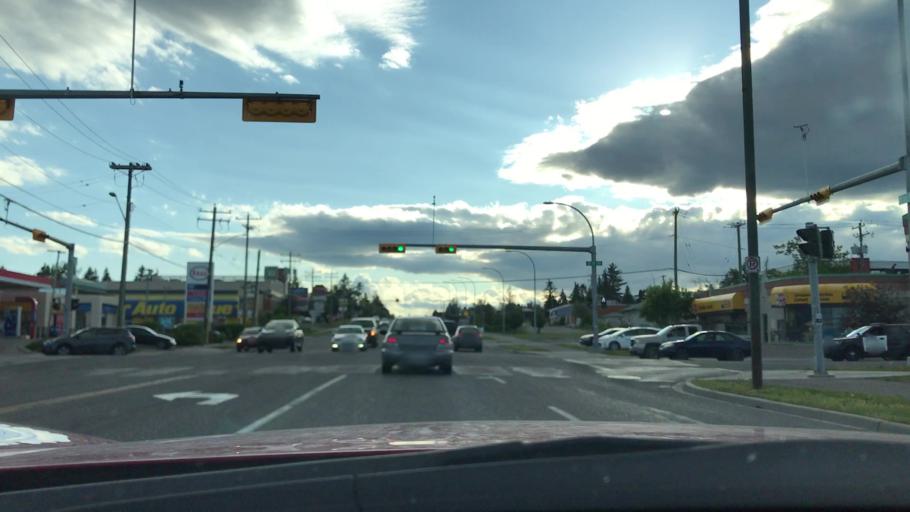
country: CA
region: Alberta
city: Calgary
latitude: 51.0378
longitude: -114.1407
